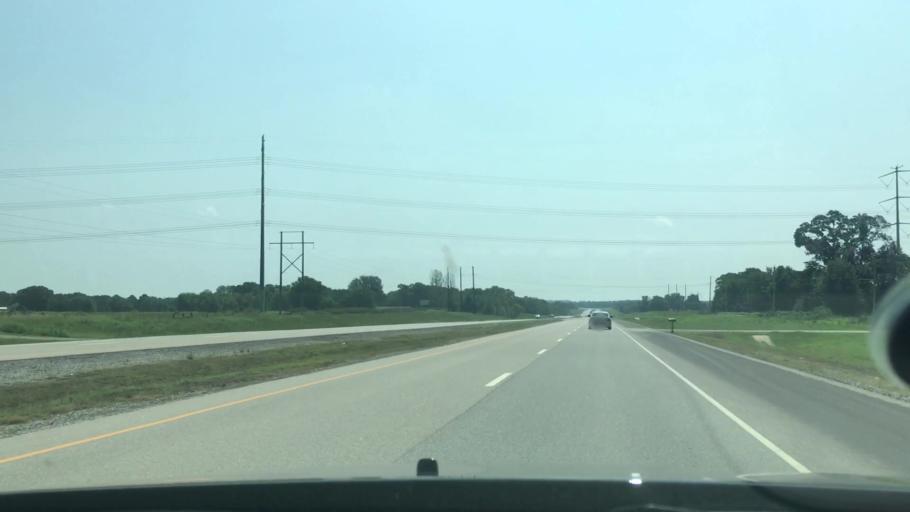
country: US
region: Oklahoma
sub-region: Atoka County
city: Atoka
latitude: 34.3326
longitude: -96.0527
